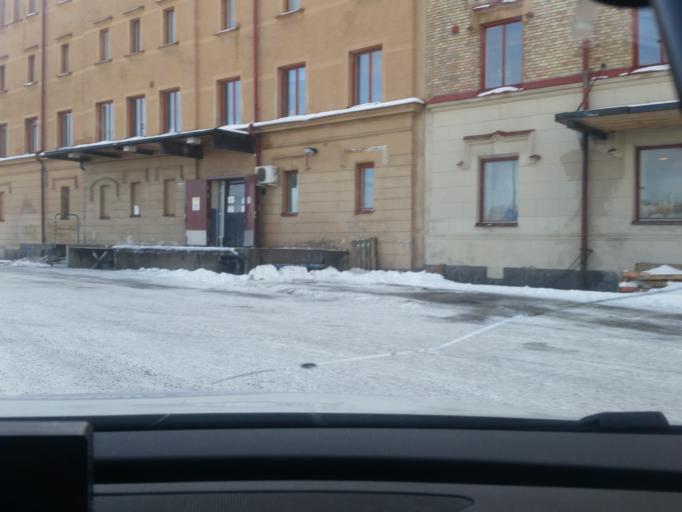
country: SE
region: Vaesternorrland
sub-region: Sundsvalls Kommun
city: Sundsvall
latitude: 62.3924
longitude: 17.3100
